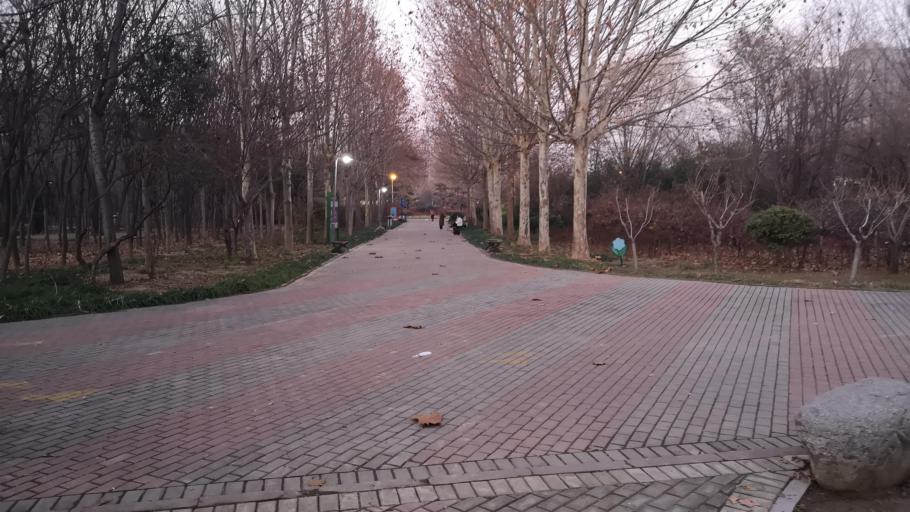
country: CN
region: Henan Sheng
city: Zhongyuanlu
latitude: 35.7425
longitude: 115.0631
